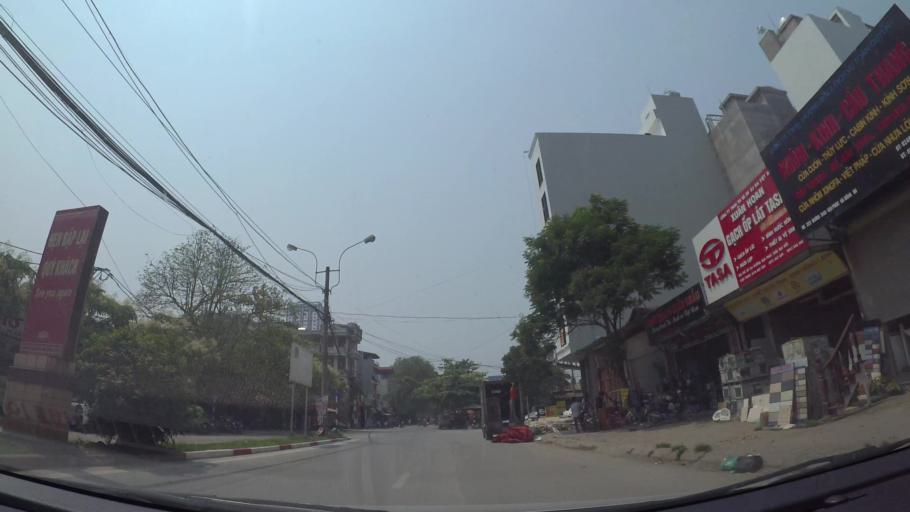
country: VN
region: Ha Noi
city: Ha Dong
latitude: 20.9839
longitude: 105.7695
